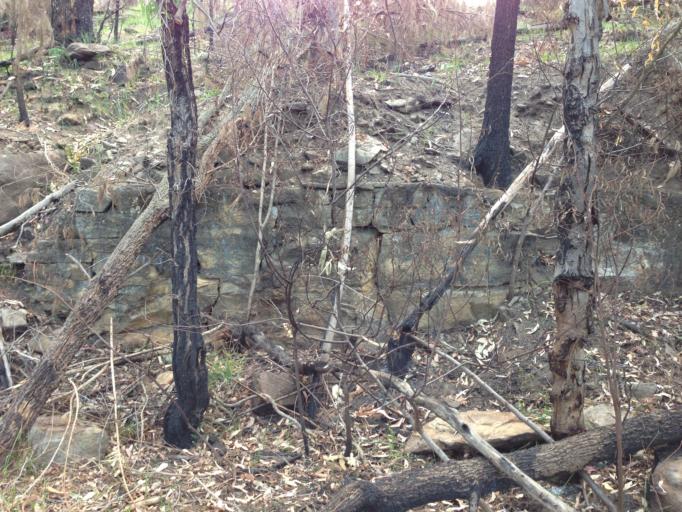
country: AU
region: New South Wales
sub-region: Blue Mountains Municipality
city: Glenbrook
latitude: -33.7611
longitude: 150.6390
